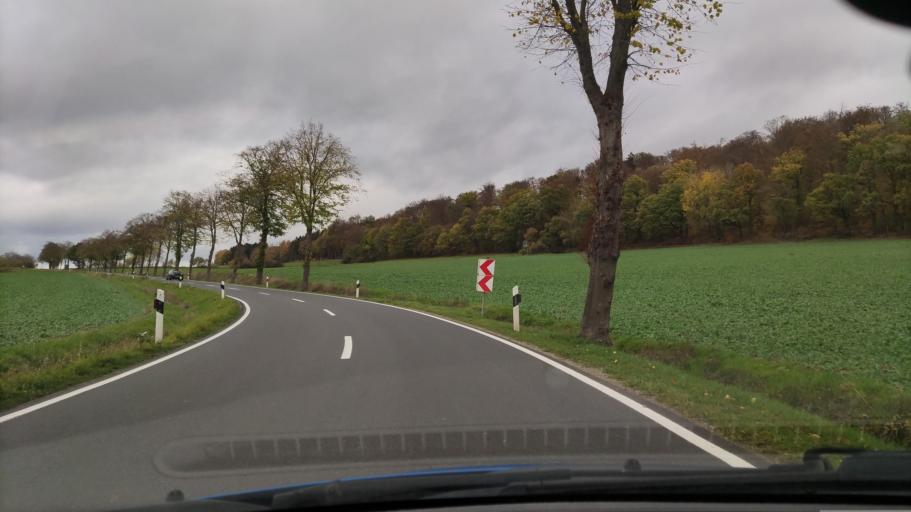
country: DE
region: Lower Saxony
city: Wangelnstedt
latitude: 51.8627
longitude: 9.7115
